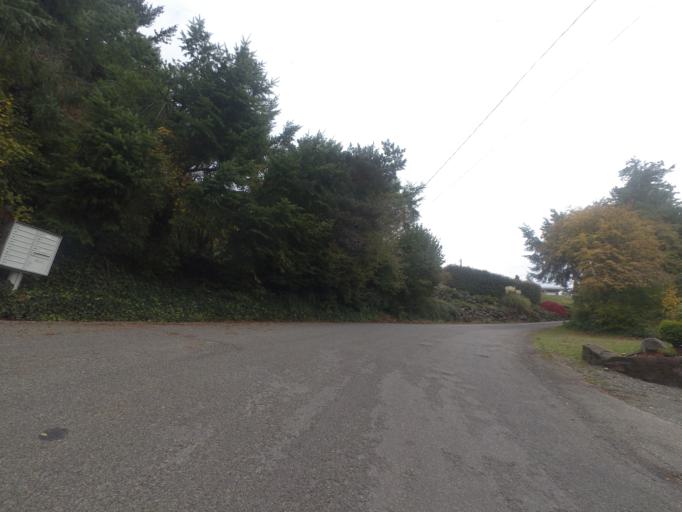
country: US
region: Washington
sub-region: Pierce County
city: University Place
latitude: 47.2172
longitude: -122.5688
